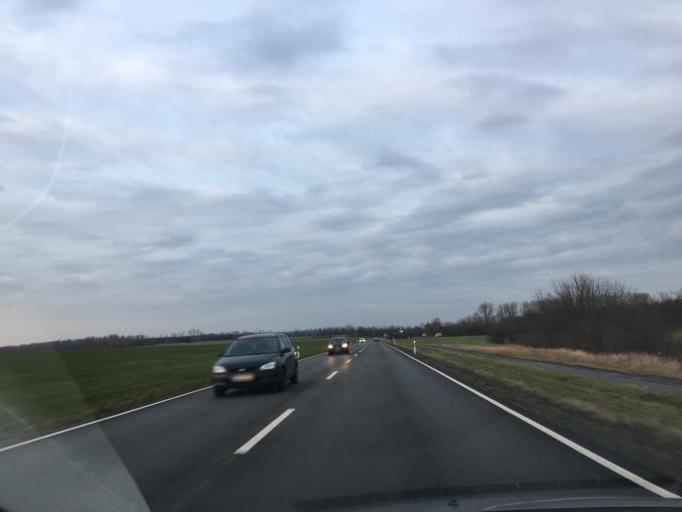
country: DE
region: Saxony
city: Regis-Breitingen
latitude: 51.0956
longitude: 12.4752
